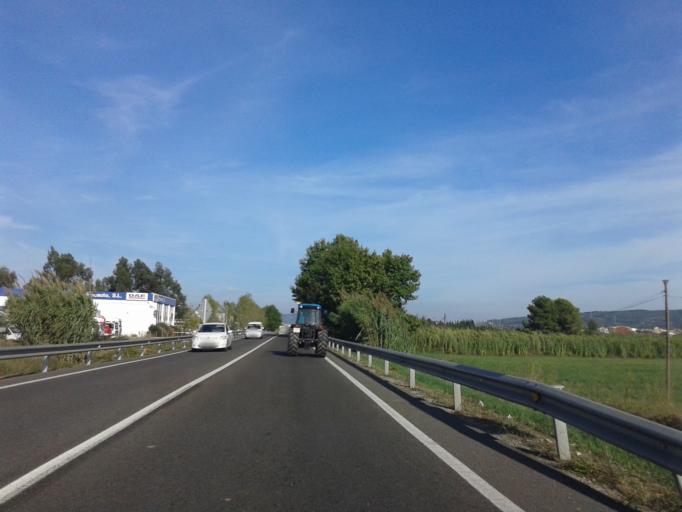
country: ES
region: Catalonia
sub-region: Provincia de Barcelona
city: Vilafranca del Penedes
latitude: 41.3513
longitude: 1.7256
